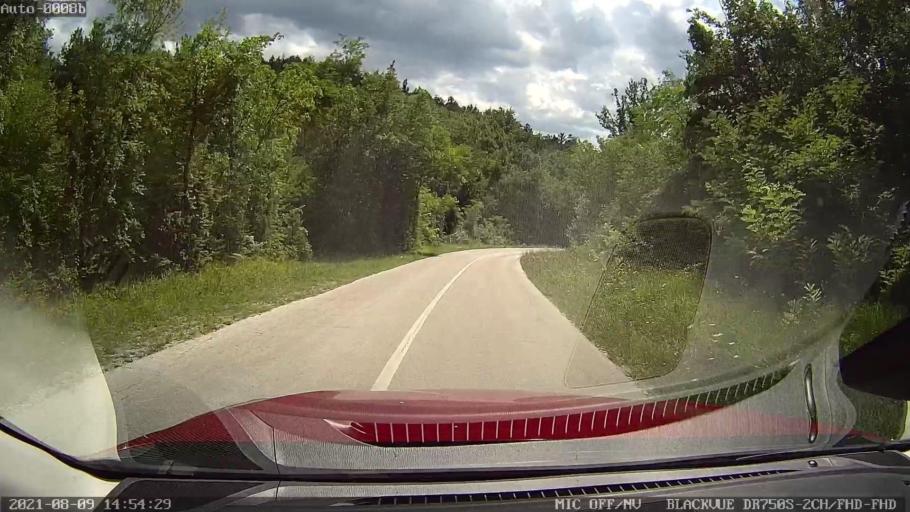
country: HR
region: Istarska
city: Pazin
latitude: 45.2790
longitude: 14.0735
